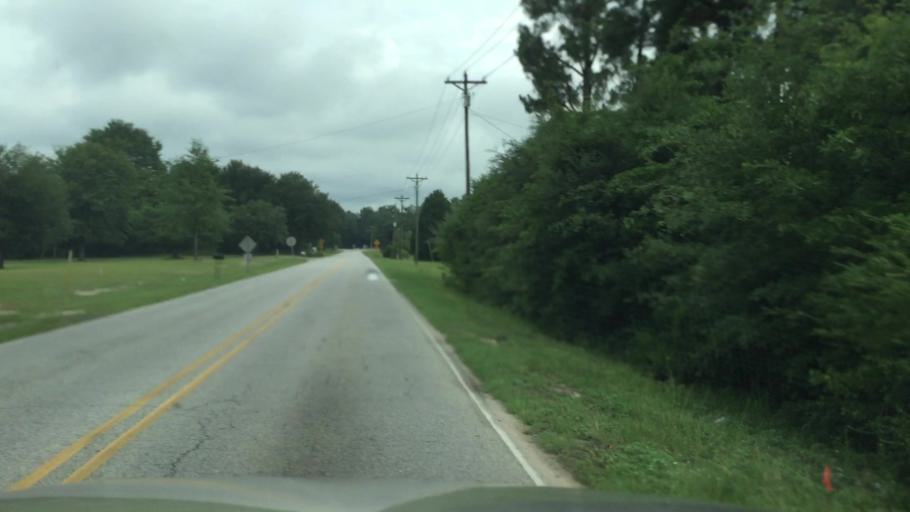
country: US
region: South Carolina
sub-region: Sumter County
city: Cane Savannah
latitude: 33.9061
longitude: -80.4082
